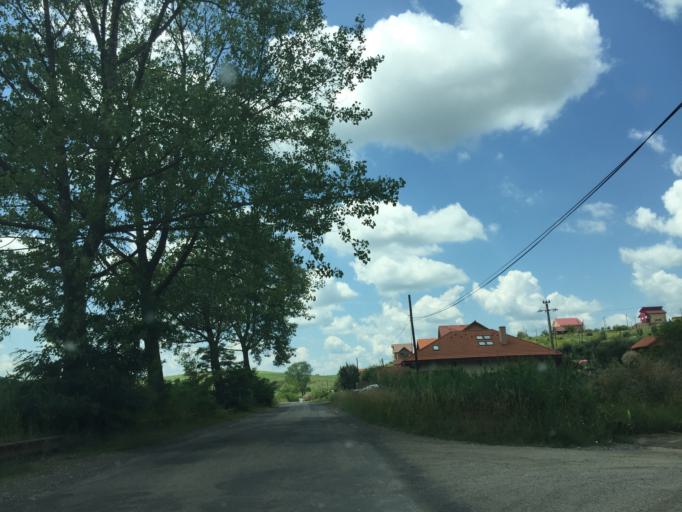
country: RO
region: Cluj
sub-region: Comuna Chinteni
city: Chinteni
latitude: 46.8754
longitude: 23.5258
